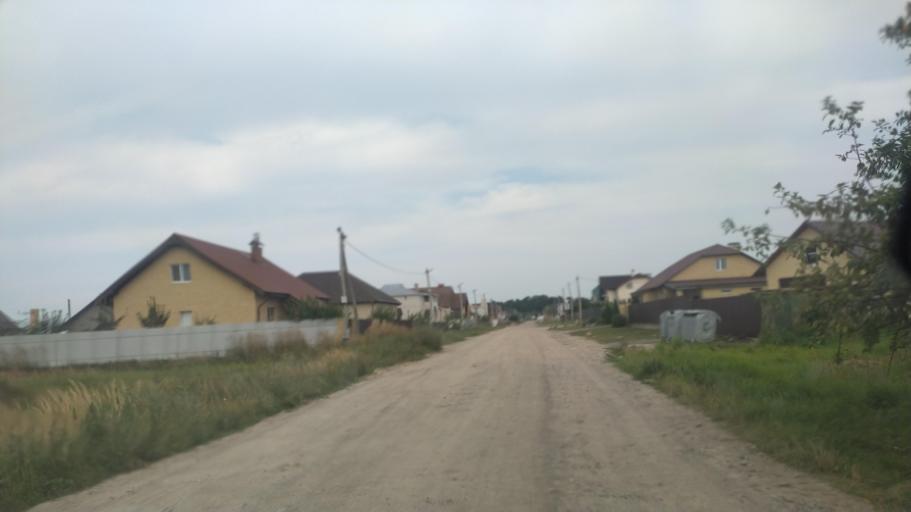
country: BY
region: Brest
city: Byaroza
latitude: 52.5419
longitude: 24.9707
